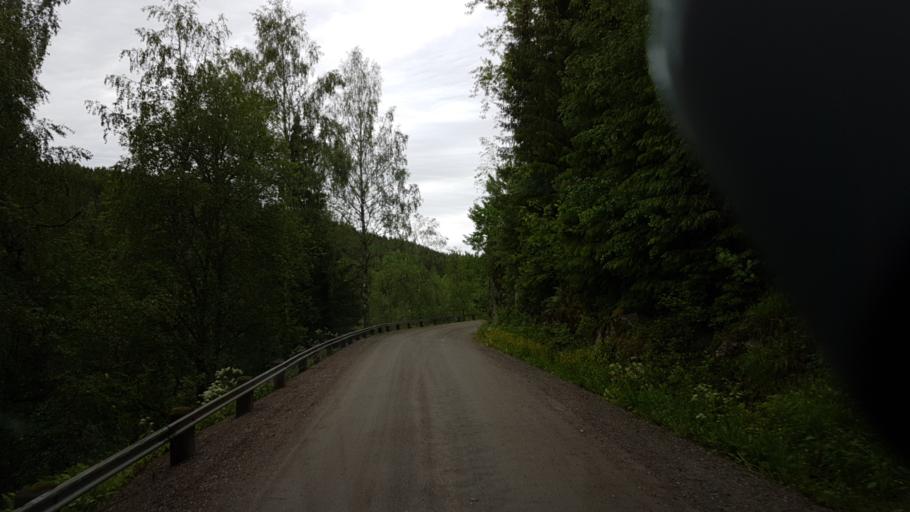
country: NO
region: Ostfold
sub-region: Romskog
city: Romskog
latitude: 59.7070
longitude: 11.9626
